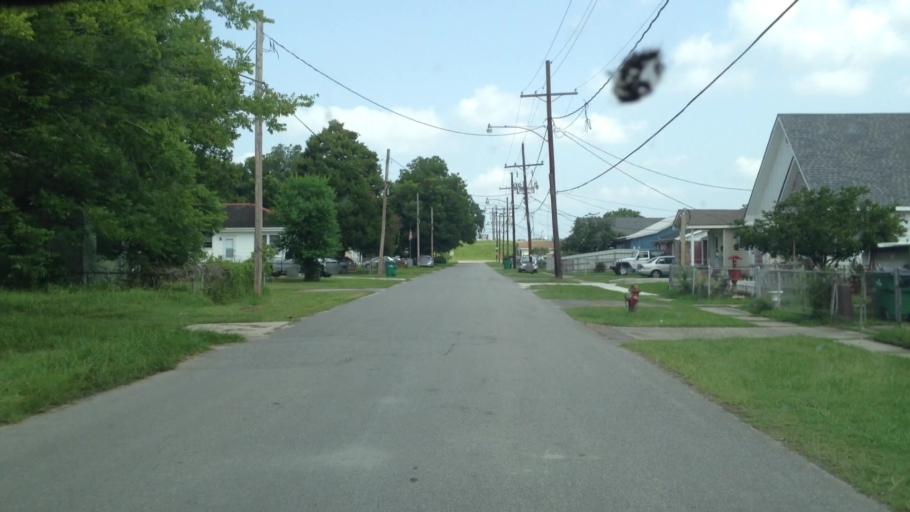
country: US
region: Louisiana
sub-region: Jefferson Parish
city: Bridge City
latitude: 29.9335
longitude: -90.1700
